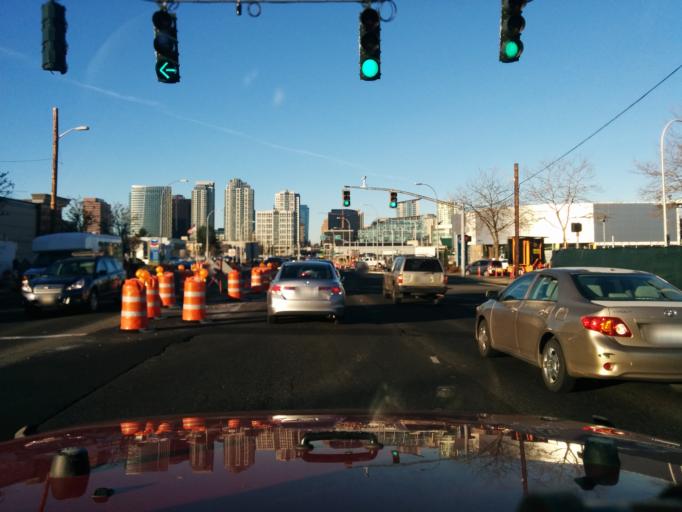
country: US
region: Washington
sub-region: King County
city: Bellevue
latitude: 47.6174
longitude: -122.1803
